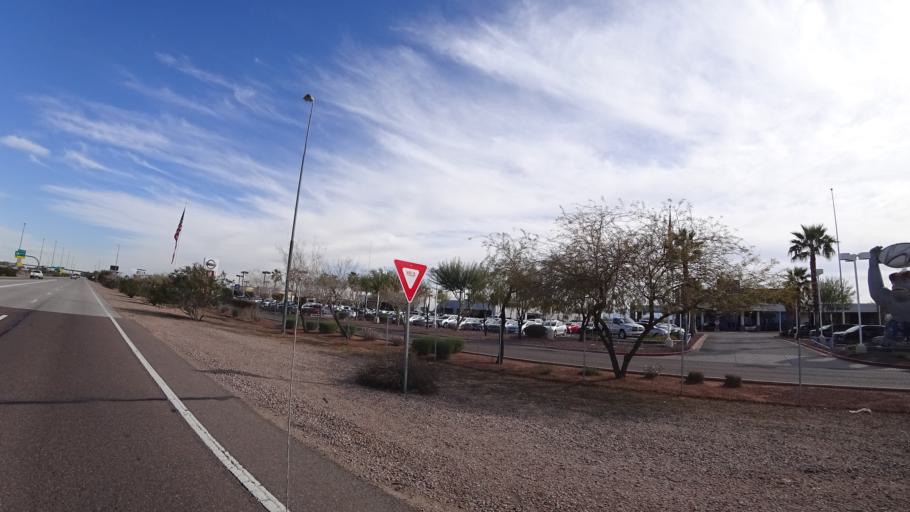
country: US
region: Arizona
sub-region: Maricopa County
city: Tolleson
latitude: 33.4608
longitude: -112.2854
